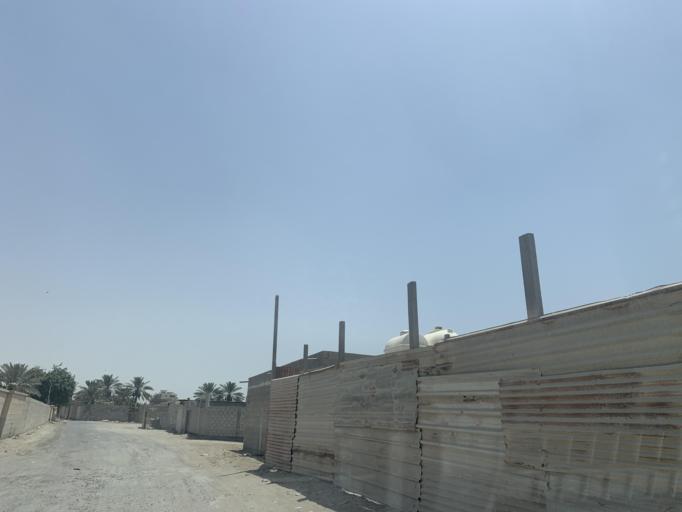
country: BH
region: Central Governorate
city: Madinat Hamad
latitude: 26.1561
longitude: 50.4960
